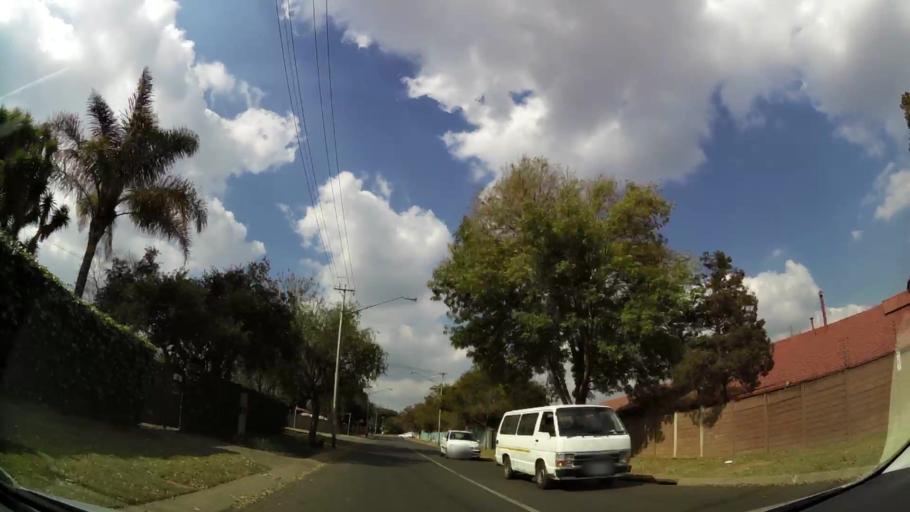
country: ZA
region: Gauteng
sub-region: City of Tshwane Metropolitan Municipality
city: Centurion
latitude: -25.8327
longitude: 28.2586
